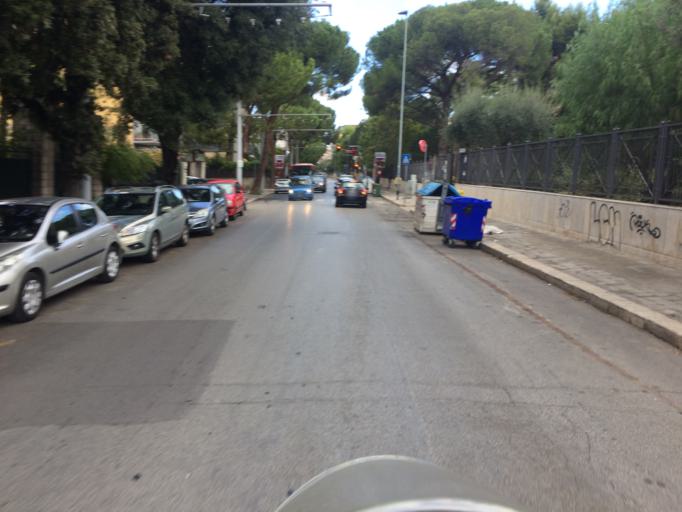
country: IT
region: Apulia
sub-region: Provincia di Bari
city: Bari
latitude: 41.0993
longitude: 16.8713
